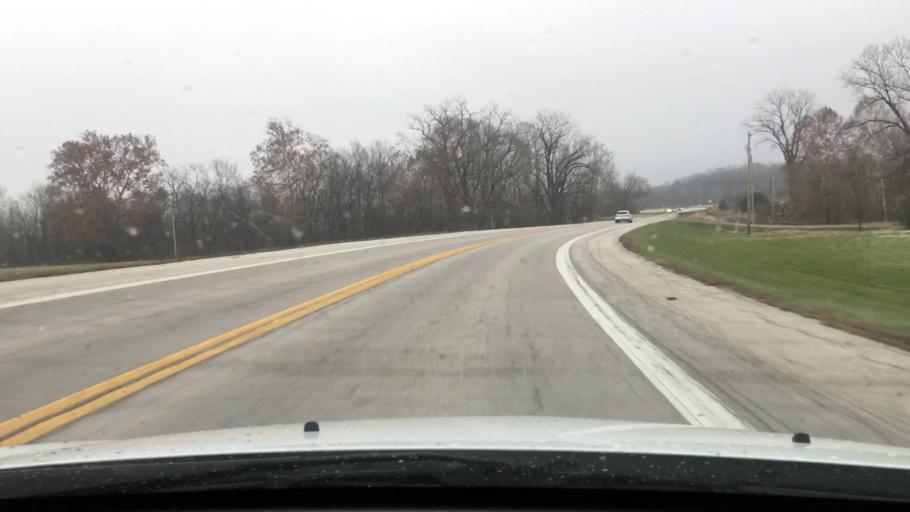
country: US
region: Missouri
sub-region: Pike County
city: Bowling Green
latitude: 39.3792
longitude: -91.1497
